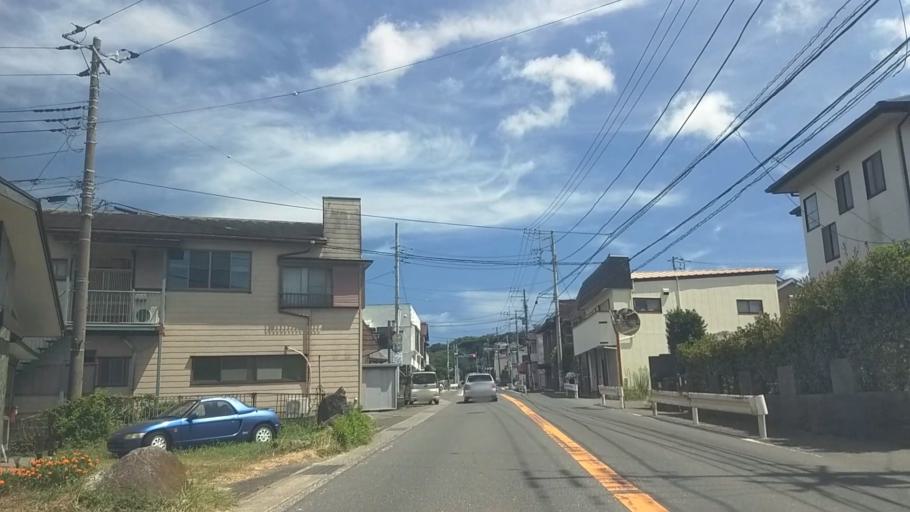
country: JP
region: Kanagawa
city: Yokosuka
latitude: 35.2187
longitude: 139.6414
